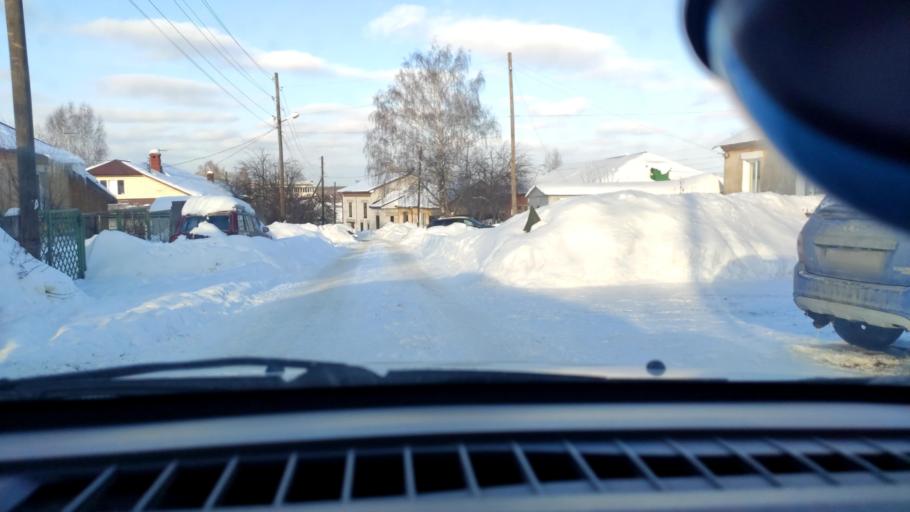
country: RU
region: Perm
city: Kultayevo
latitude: 57.9368
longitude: 55.8577
